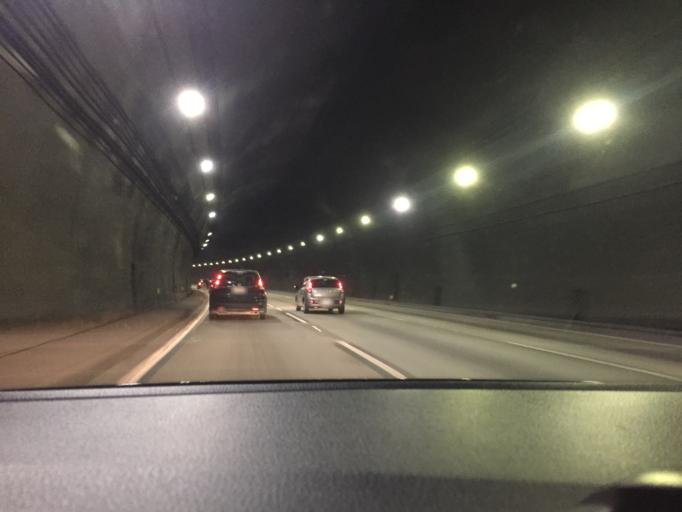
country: BR
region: Sao Paulo
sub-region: Cubatao
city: Cubatao
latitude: -23.8899
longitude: -46.5032
